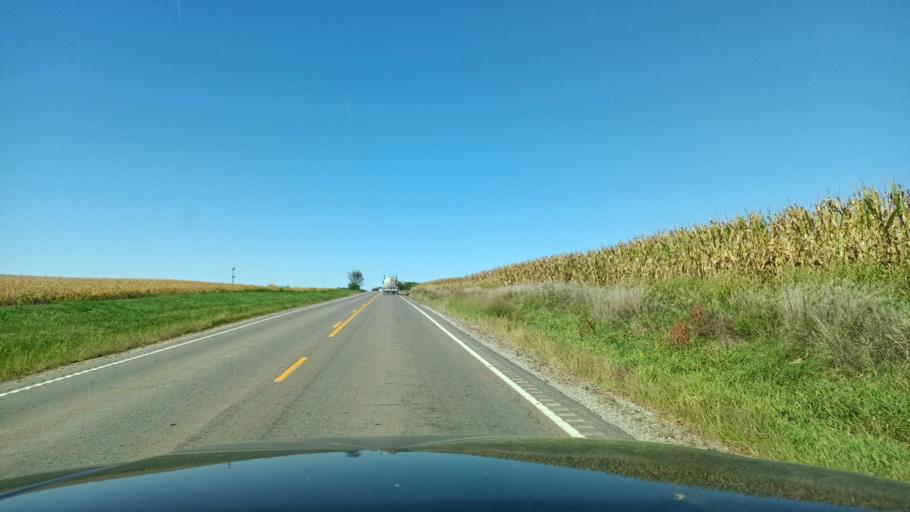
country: US
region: Missouri
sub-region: Scotland County
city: Memphis
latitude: 40.4557
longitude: -92.0783
